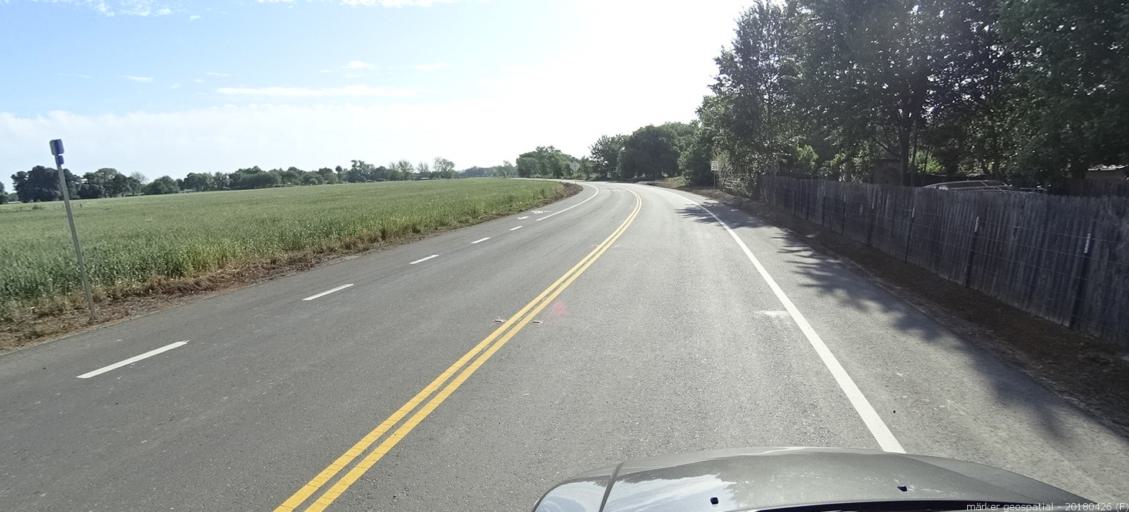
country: US
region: California
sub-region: Yolo County
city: West Sacramento
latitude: 38.5199
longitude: -121.5558
